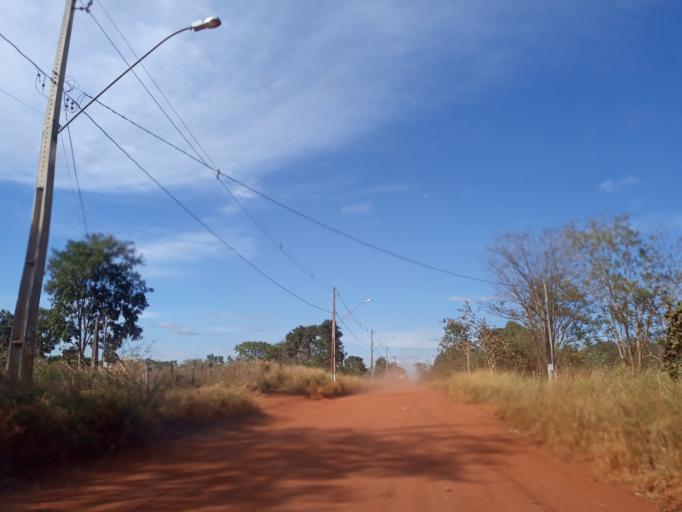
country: BR
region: Minas Gerais
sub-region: Ituiutaba
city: Ituiutaba
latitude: -18.9559
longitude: -49.4863
